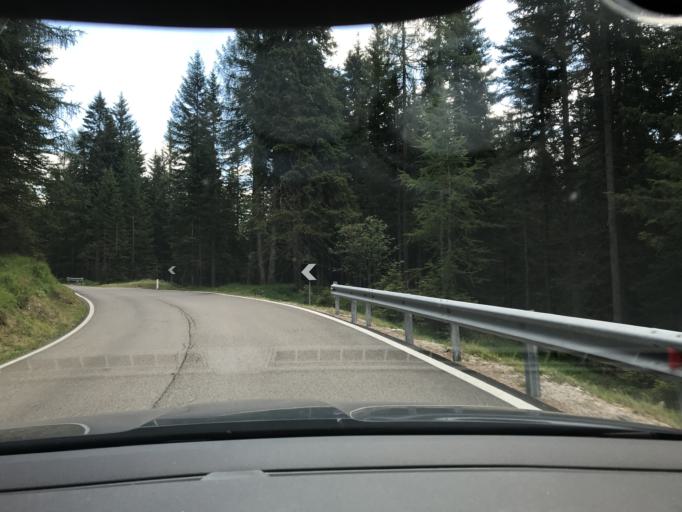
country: IT
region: Veneto
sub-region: Provincia di Belluno
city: Cortina d'Ampezzo
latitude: 46.5570
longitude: 12.2221
